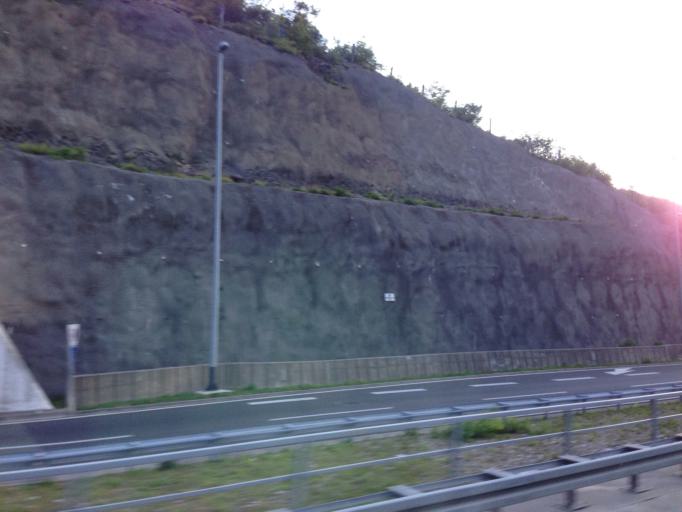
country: HR
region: Primorsko-Goranska
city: Cernik
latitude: 45.3209
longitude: 14.4964
